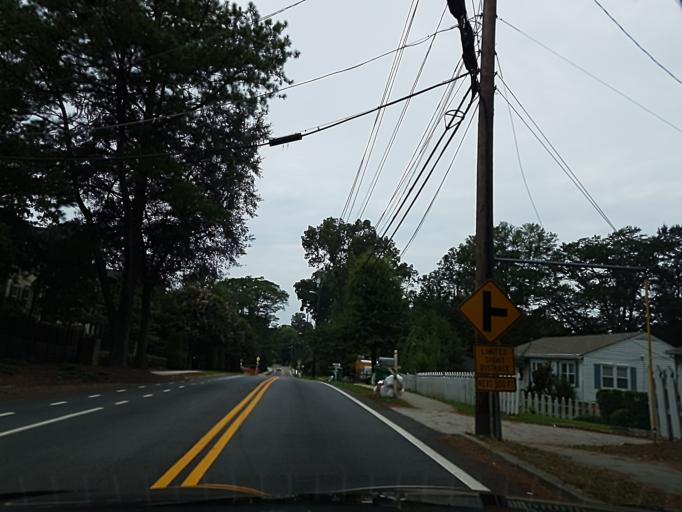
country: US
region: Georgia
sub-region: DeKalb County
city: North Atlanta
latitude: 33.8471
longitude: -84.3285
